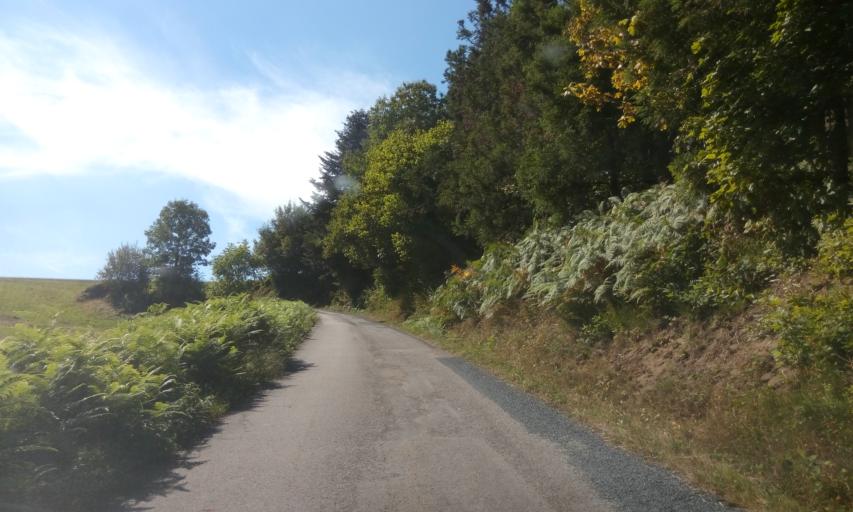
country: FR
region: Rhone-Alpes
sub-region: Departement du Rhone
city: Cublize
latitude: 45.9823
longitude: 4.3889
